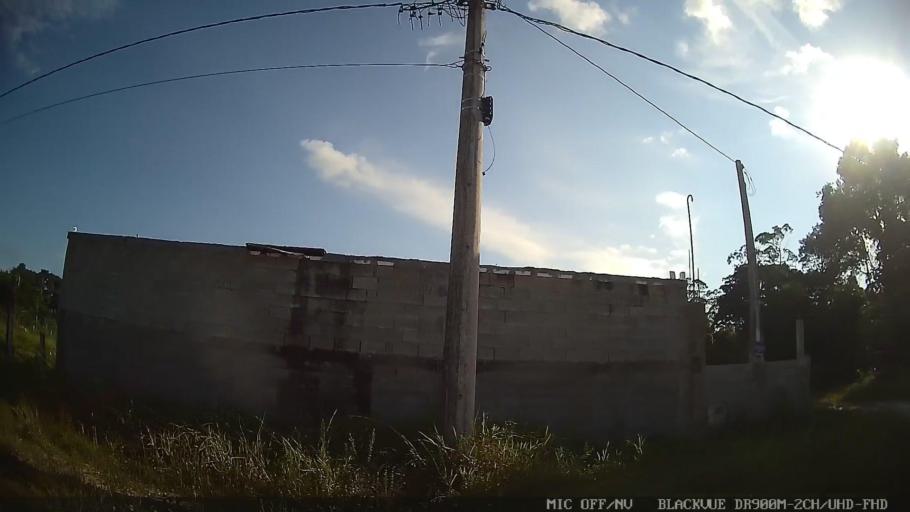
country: BR
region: Sao Paulo
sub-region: Itanhaem
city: Itanhaem
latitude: -24.1713
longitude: -46.8198
